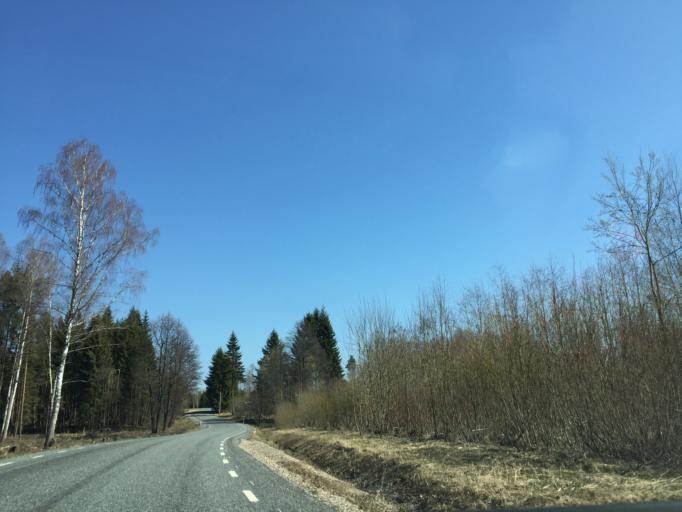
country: EE
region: Tartu
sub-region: Alatskivi vald
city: Kallaste
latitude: 58.5872
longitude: 27.0568
